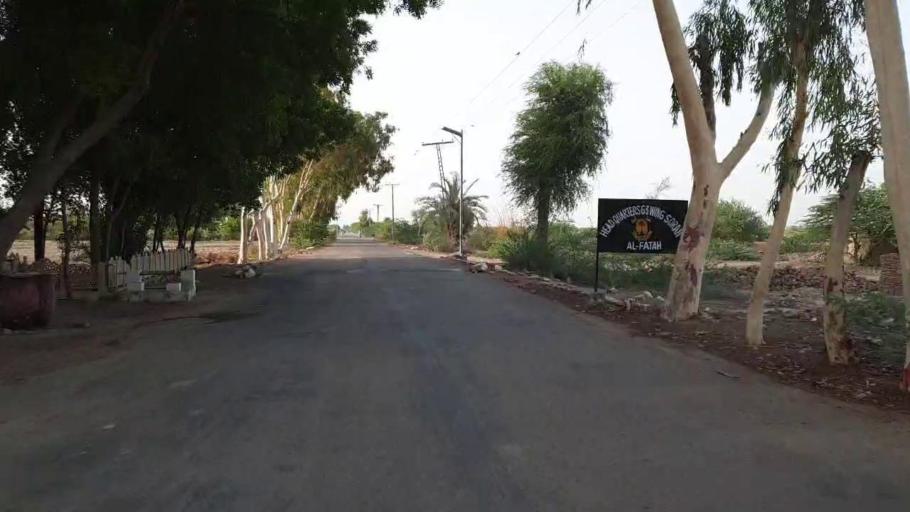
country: PK
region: Sindh
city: Bozdar
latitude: 27.1215
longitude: 68.9563
